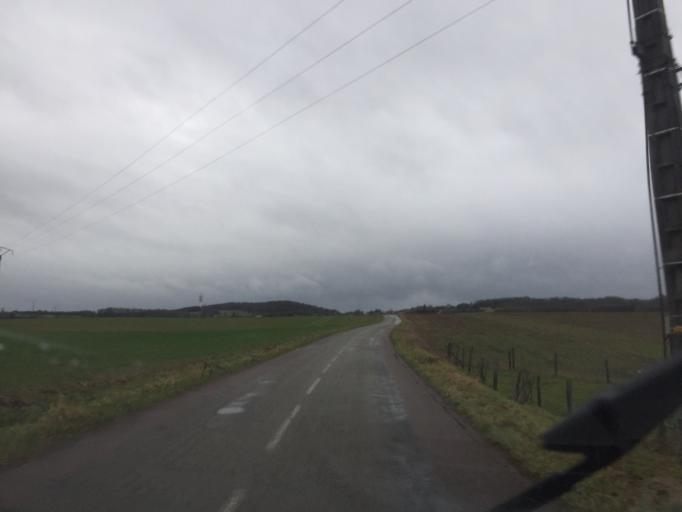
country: FR
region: Franche-Comte
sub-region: Departement du Jura
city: Dole
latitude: 47.1436
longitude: 5.5364
